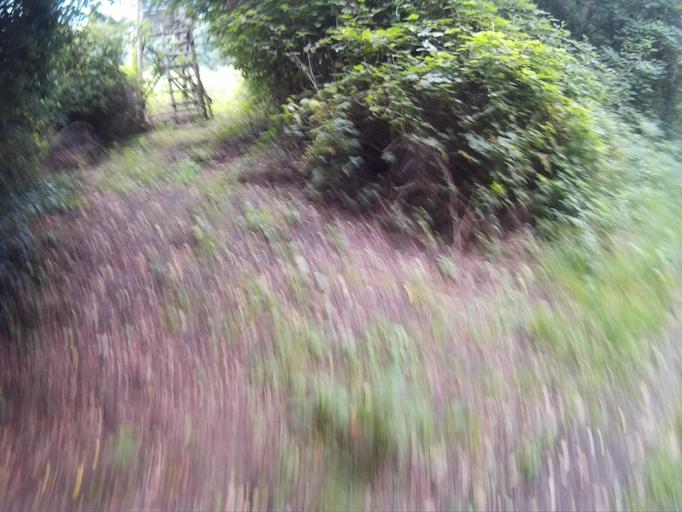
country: HU
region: Veszprem
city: Papa
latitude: 47.2807
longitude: 17.5571
